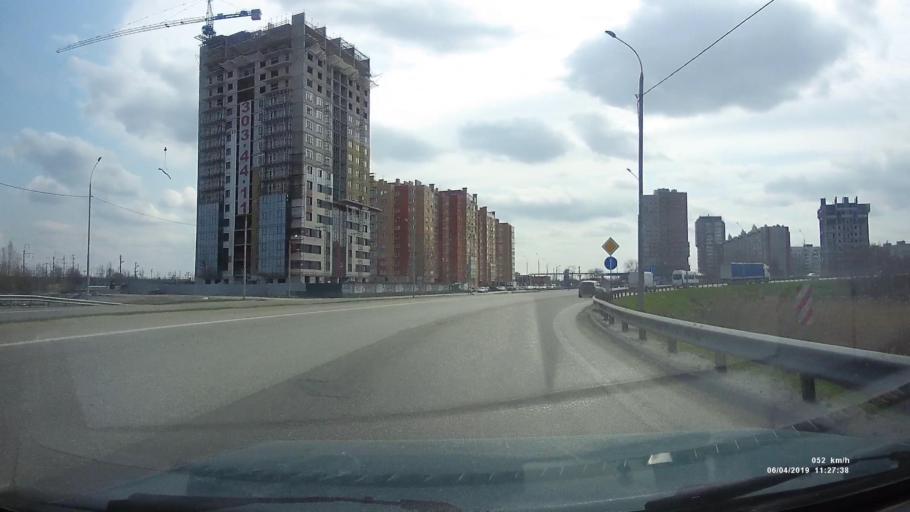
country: RU
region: Rostov
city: Bataysk
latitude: 47.1584
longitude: 39.7430
